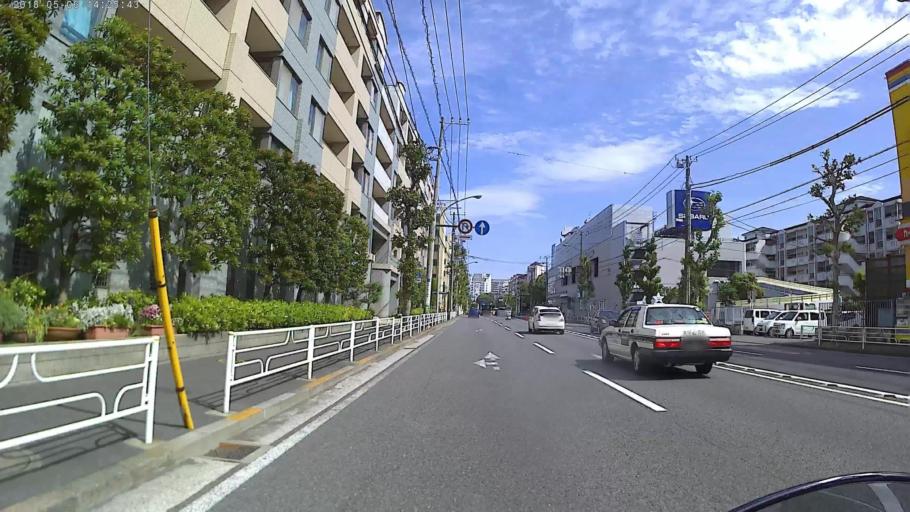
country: JP
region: Kanagawa
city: Yokohama
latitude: 35.4390
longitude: 139.6589
